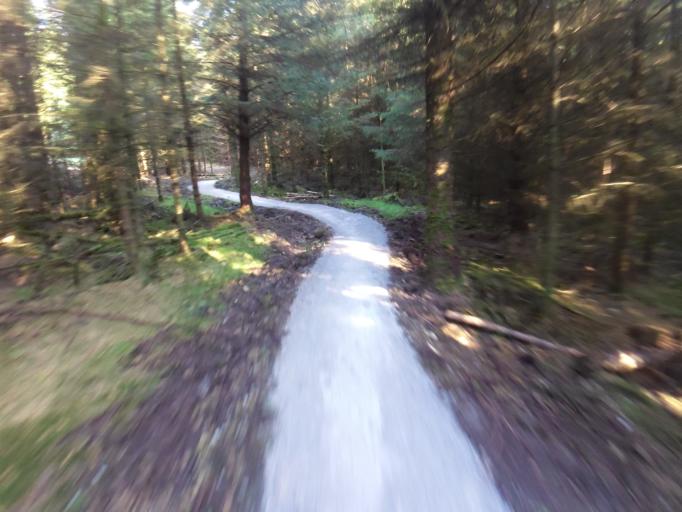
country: GB
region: England
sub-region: North Yorkshire
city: Settle
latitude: 54.0050
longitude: -2.3880
